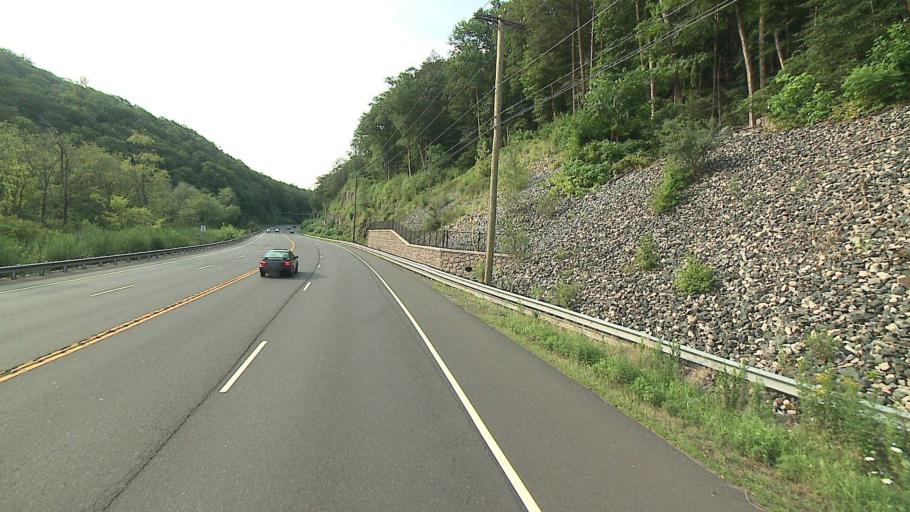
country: US
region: Connecticut
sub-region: Fairfield County
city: Danbury
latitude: 41.3576
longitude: -73.4717
